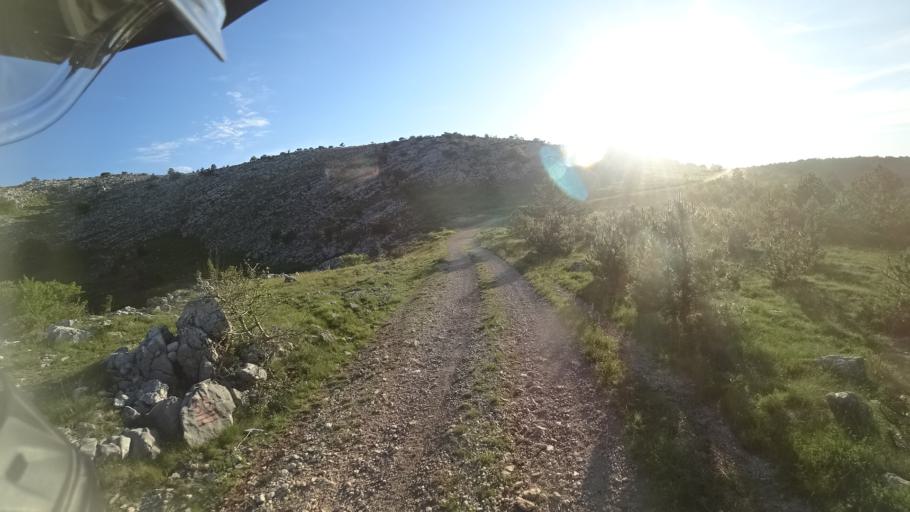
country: HR
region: Sibensko-Kniniska
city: Drnis
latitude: 43.8772
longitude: 16.3498
